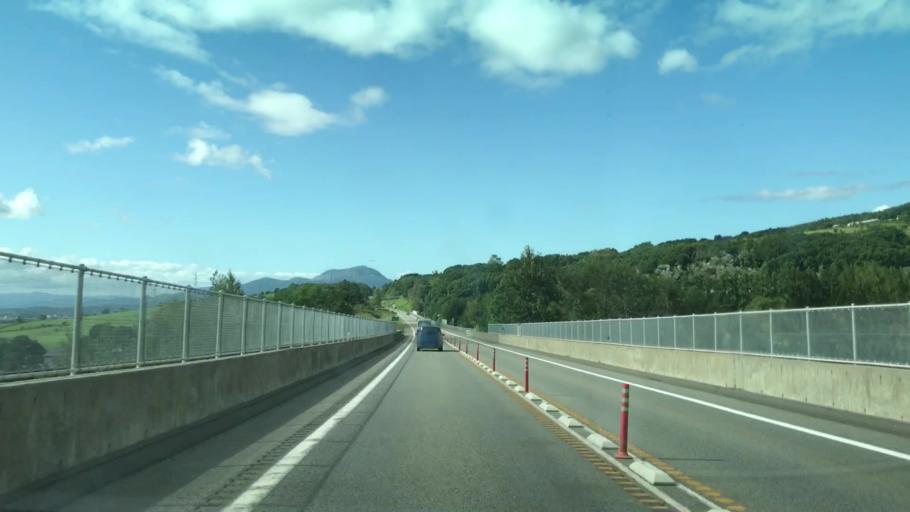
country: JP
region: Hokkaido
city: Date
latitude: 42.4318
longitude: 140.9244
